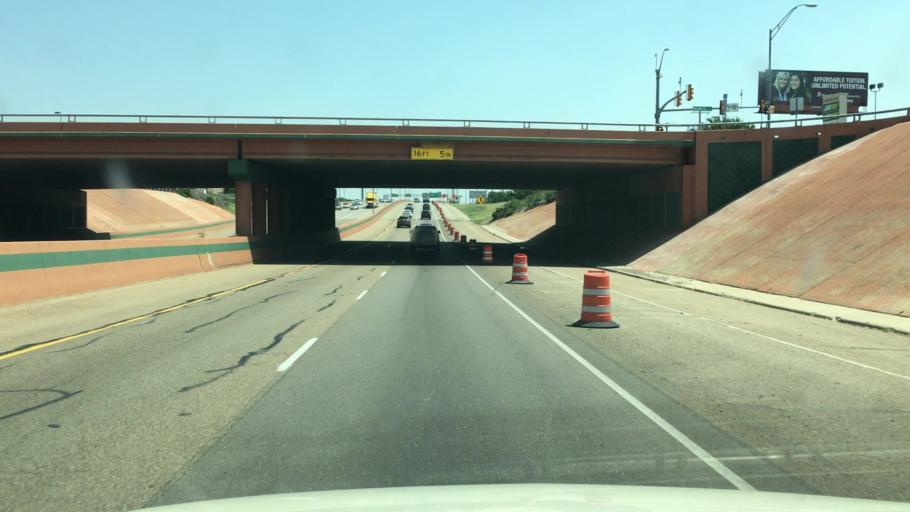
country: US
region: Texas
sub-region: Potter County
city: Amarillo
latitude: 35.1945
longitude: -101.8493
